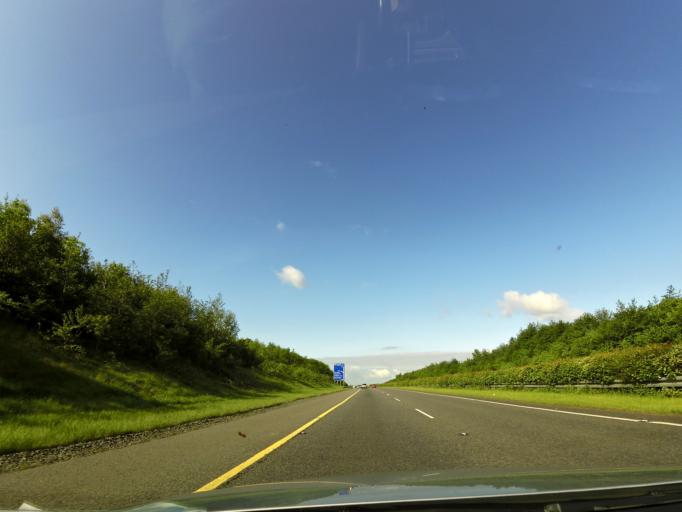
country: IE
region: Munster
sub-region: County Limerick
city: Annacotty
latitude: 52.6555
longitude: -8.5484
